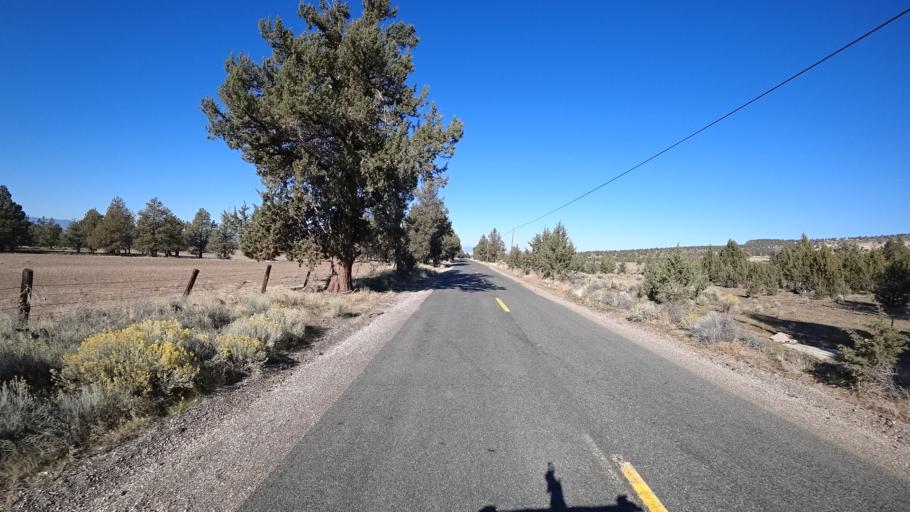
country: US
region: California
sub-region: Siskiyou County
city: Montague
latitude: 41.6332
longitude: -122.3366
